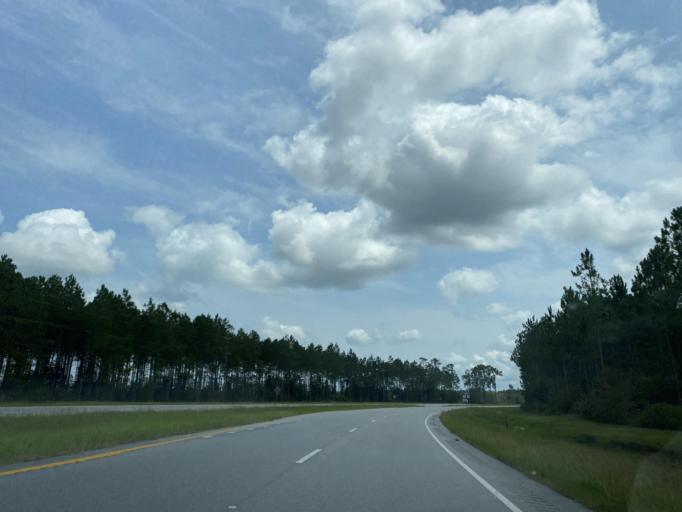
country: US
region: Georgia
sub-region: Ware County
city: Deenwood
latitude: 31.2694
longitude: -82.4340
